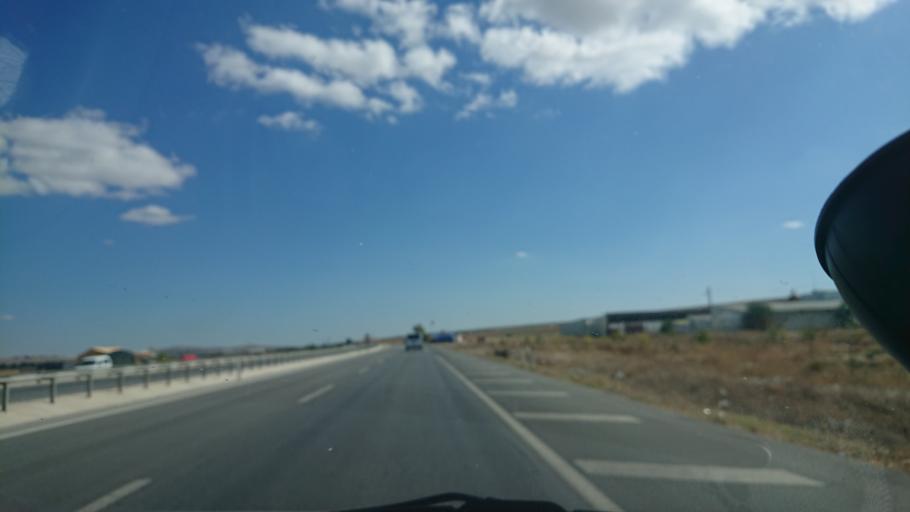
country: TR
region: Eskisehir
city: Mahmudiye
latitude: 39.5340
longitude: 30.9460
